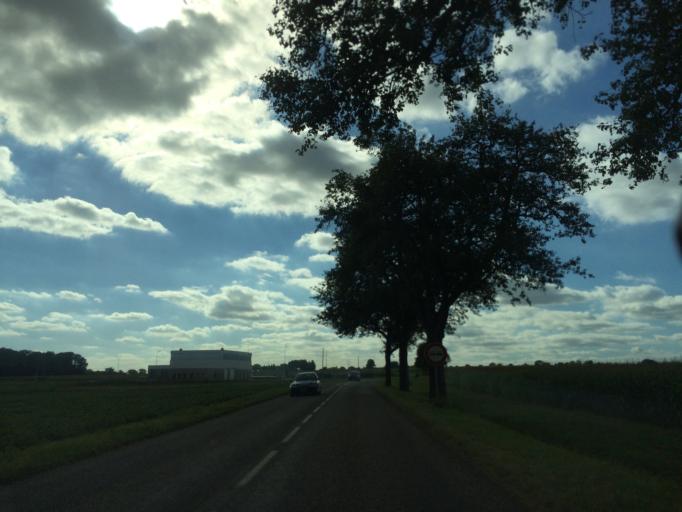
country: FR
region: Alsace
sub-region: Departement du Bas-Rhin
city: Betschdorf
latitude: 48.8971
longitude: 7.9420
